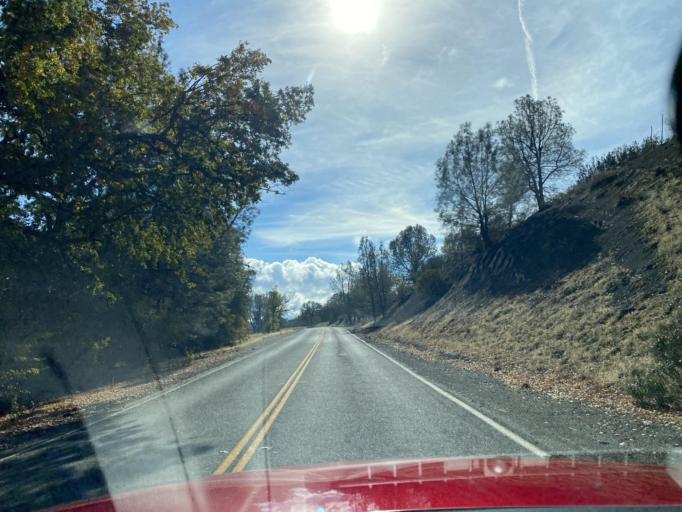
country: US
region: California
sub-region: Glenn County
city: Willows
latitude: 39.4443
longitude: -122.5133
